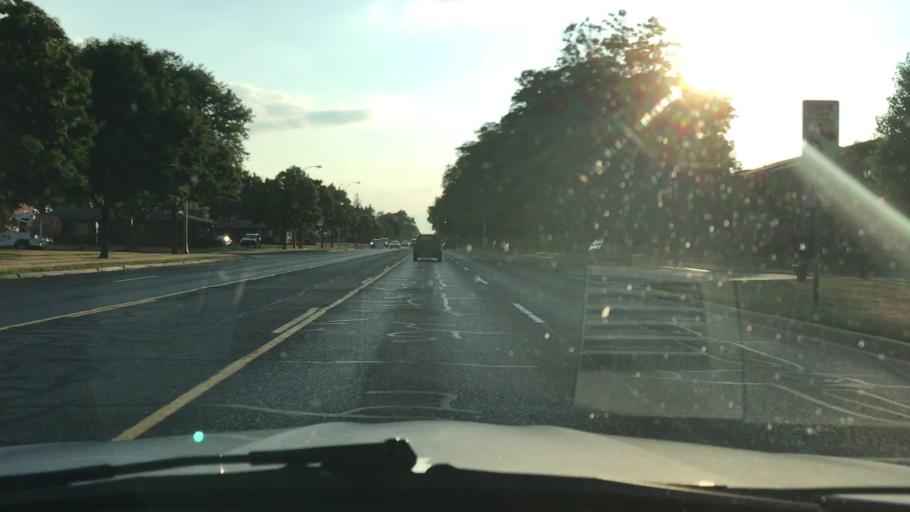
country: US
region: Michigan
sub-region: Oakland County
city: Berkley
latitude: 42.5182
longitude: -83.1726
